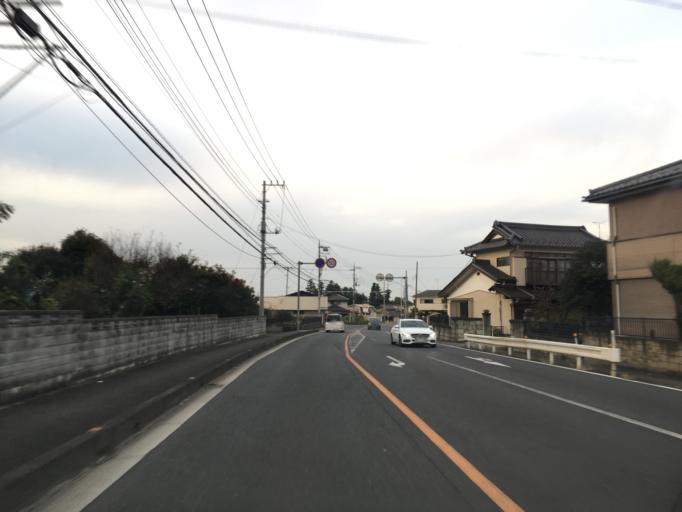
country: JP
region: Saitama
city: Sayama
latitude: 35.8742
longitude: 139.3793
